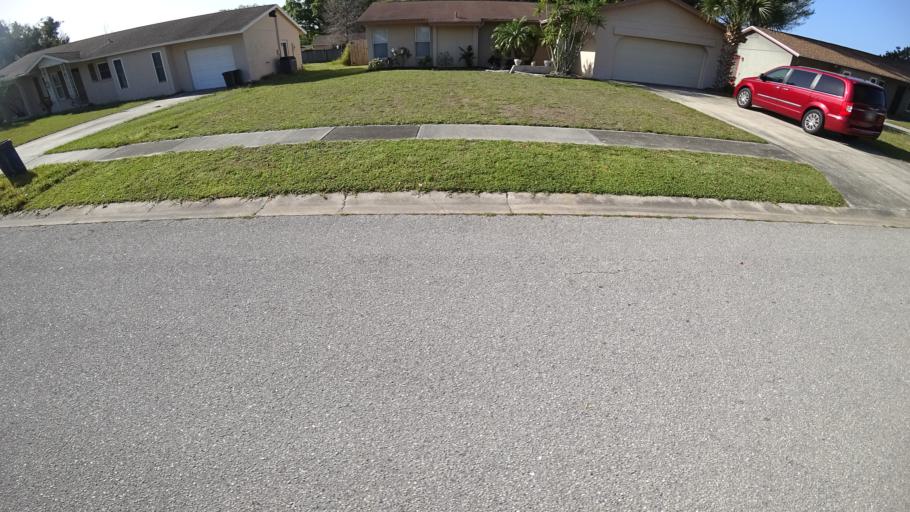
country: US
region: Florida
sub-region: Manatee County
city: Whitfield
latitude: 27.4133
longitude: -82.5567
